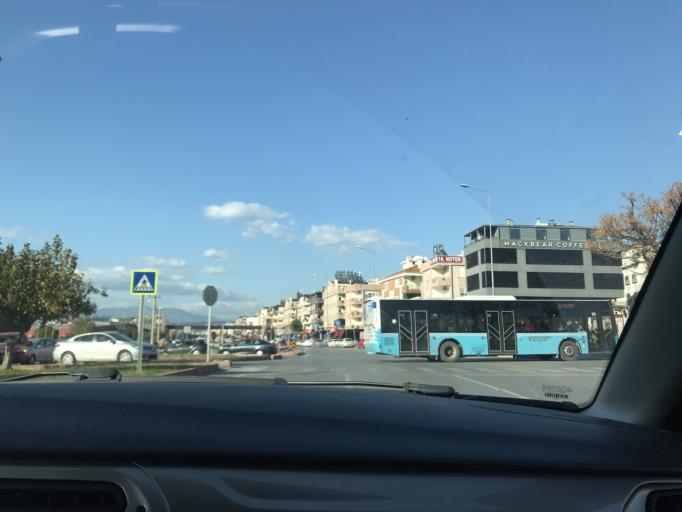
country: TR
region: Antalya
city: Antalya
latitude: 36.9018
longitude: 30.6524
